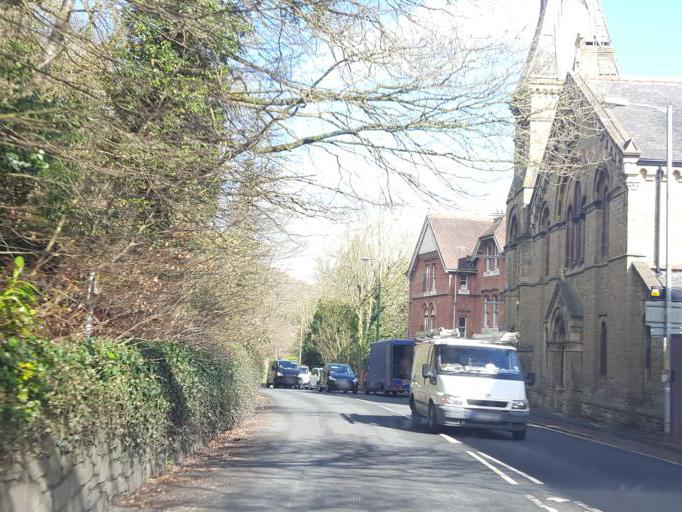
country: GB
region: England
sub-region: Worcestershire
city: Great Malvern
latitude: 52.1056
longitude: -2.3297
